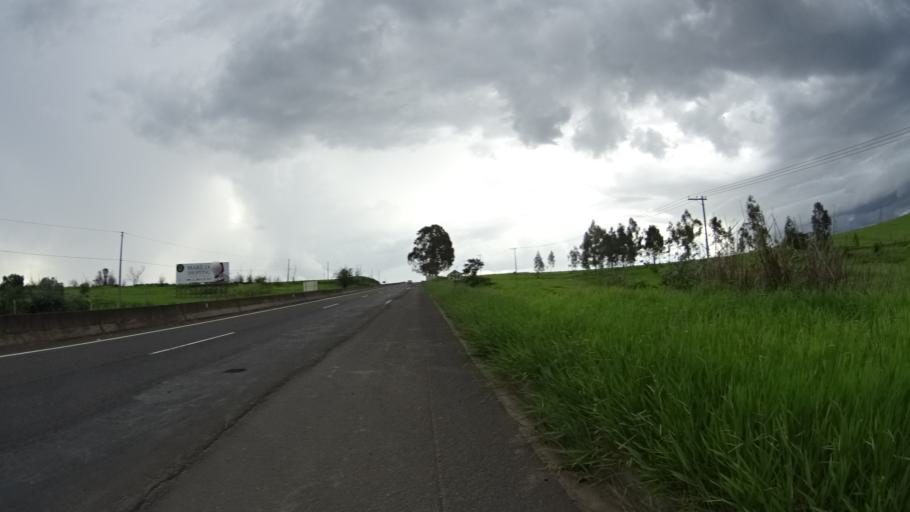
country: BR
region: Sao Paulo
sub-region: Marilia
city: Marilia
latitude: -22.2190
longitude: -49.8646
